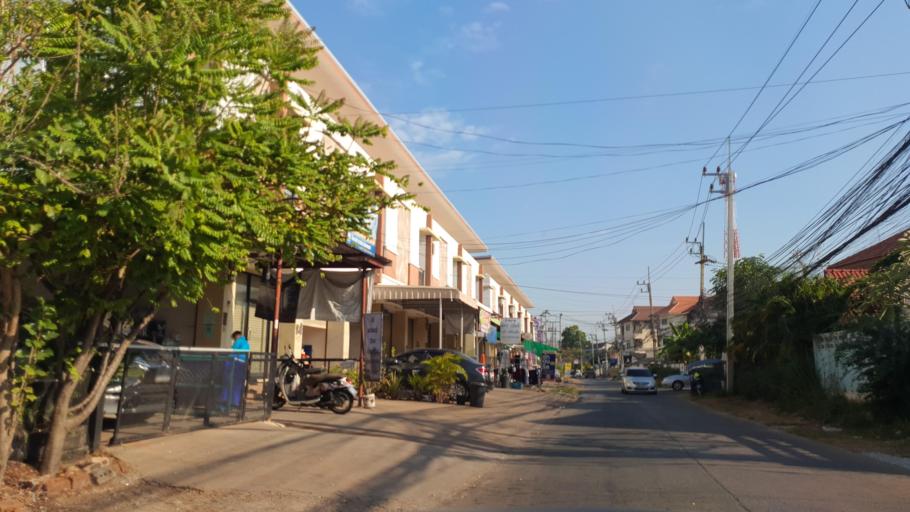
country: TH
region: Khon Kaen
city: Khon Kaen
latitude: 16.4191
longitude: 102.8050
